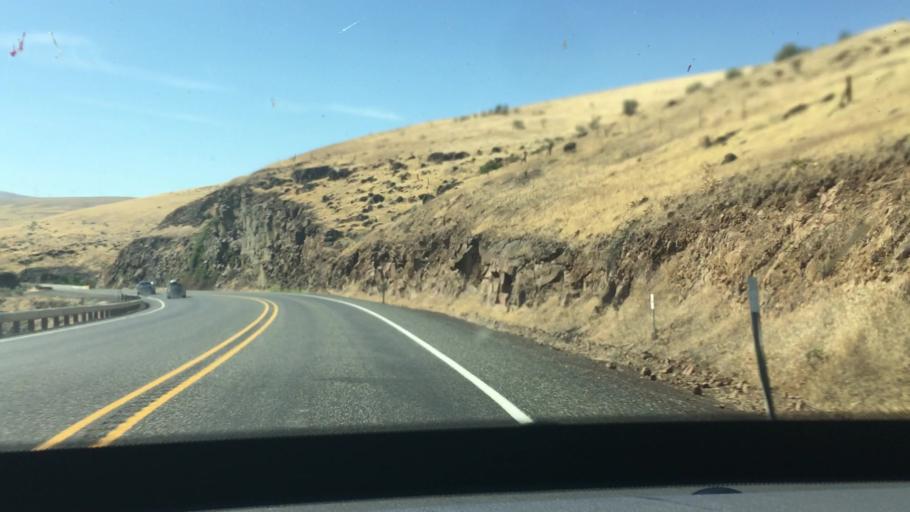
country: US
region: Oregon
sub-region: Sherman County
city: Moro
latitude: 45.6425
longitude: -120.7847
